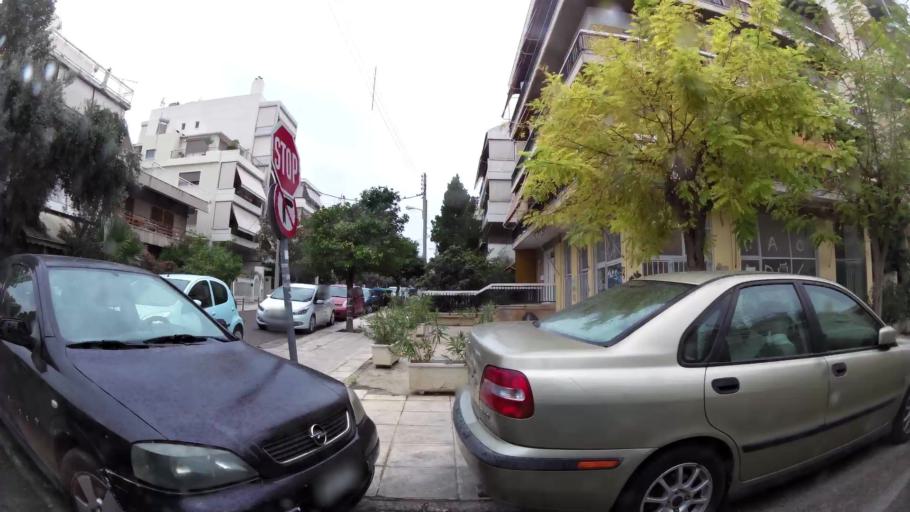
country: GR
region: Attica
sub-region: Nomarchia Athinas
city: Palaio Faliro
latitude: 37.9296
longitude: 23.7013
